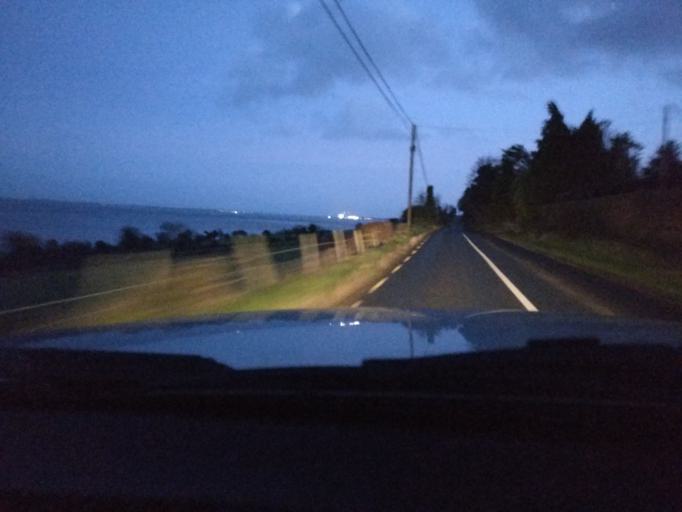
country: IE
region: Leinster
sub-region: Lu
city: Carlingford
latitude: 54.0601
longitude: -6.2050
